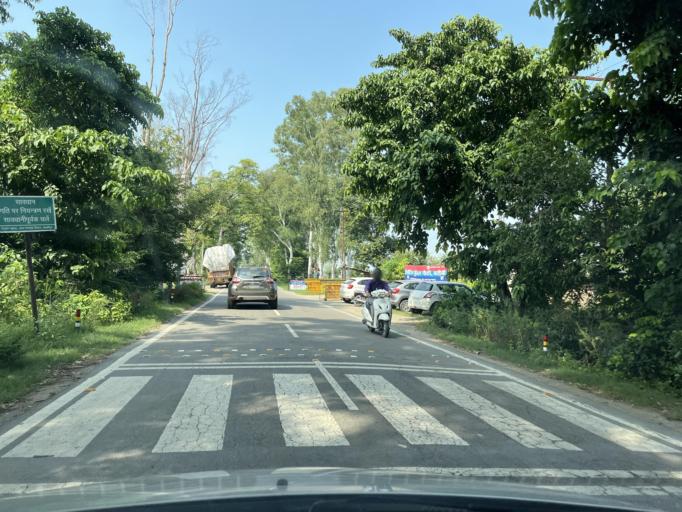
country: IN
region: Uttarakhand
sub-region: Udham Singh Nagar
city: Bazpur
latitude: 29.2127
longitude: 79.2201
